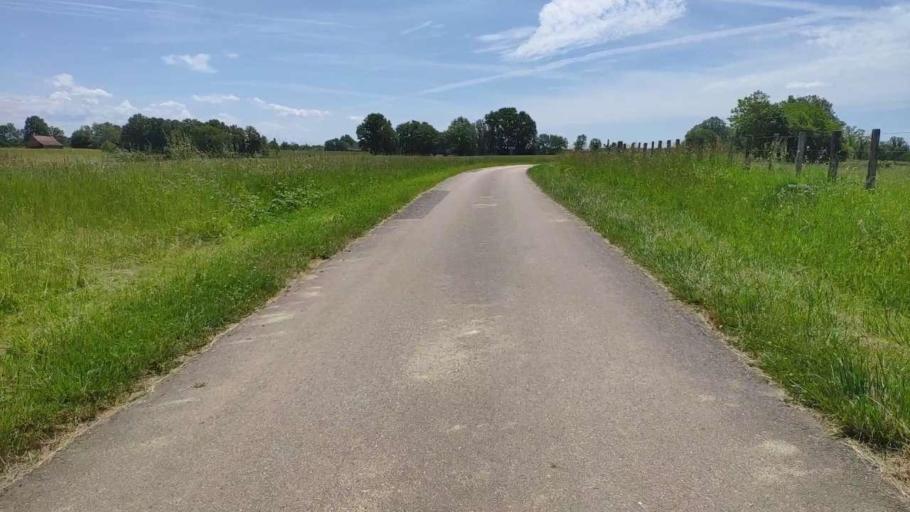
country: FR
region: Franche-Comte
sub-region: Departement du Jura
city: Bletterans
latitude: 46.7985
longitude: 5.3741
